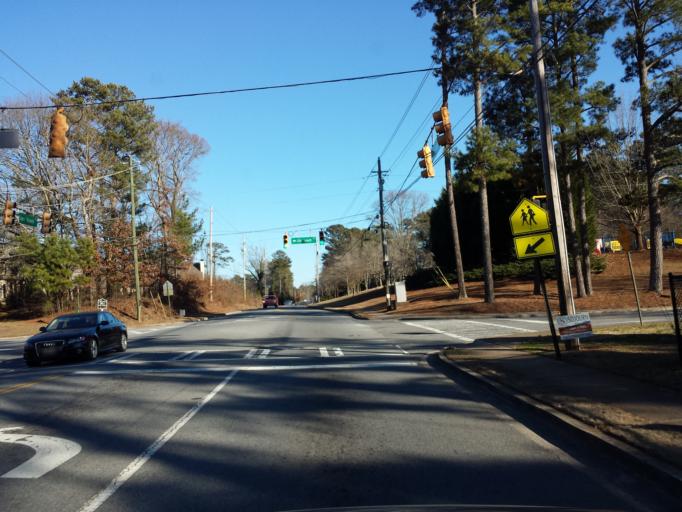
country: US
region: Georgia
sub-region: Cobb County
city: Marietta
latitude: 33.9469
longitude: -84.4865
